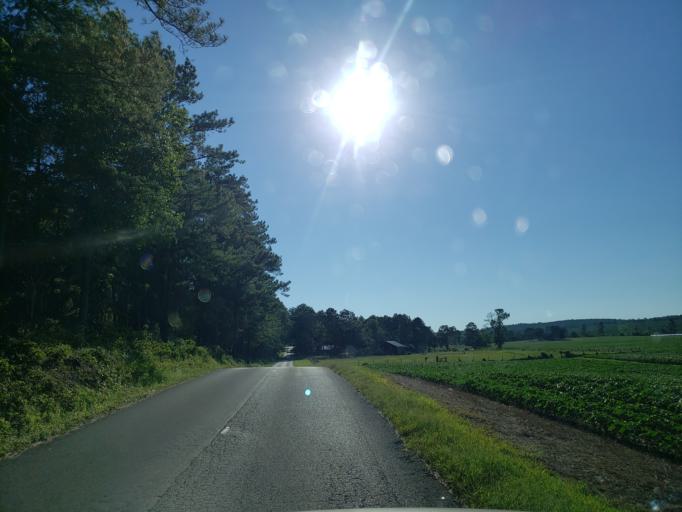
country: US
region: Georgia
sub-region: Polk County
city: Aragon
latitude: 34.1227
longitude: -85.0220
